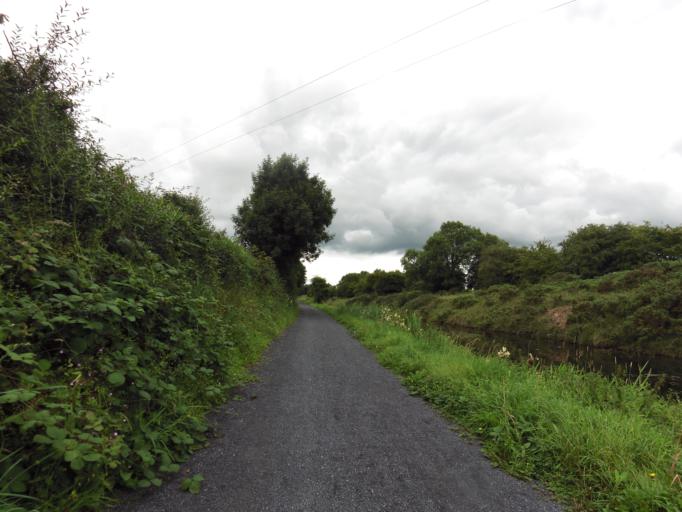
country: IE
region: Leinster
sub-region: An Iarmhi
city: An Muileann gCearr
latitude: 53.5240
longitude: -7.4450
